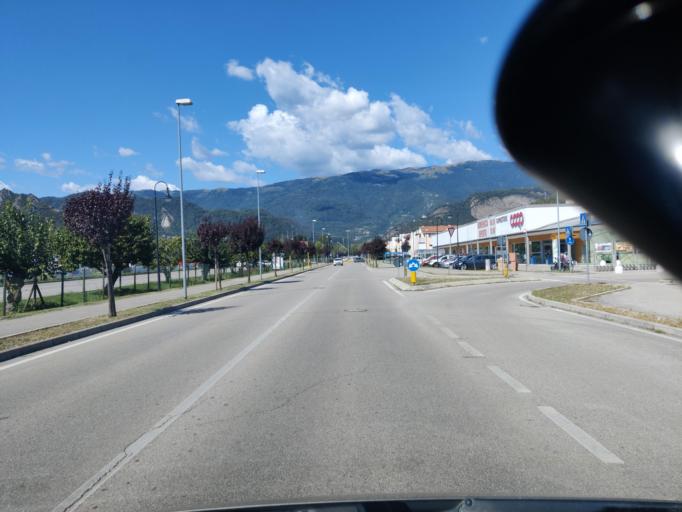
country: IT
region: Veneto
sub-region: Provincia di Treviso
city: Vittorio Veneto
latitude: 45.9814
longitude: 12.3153
